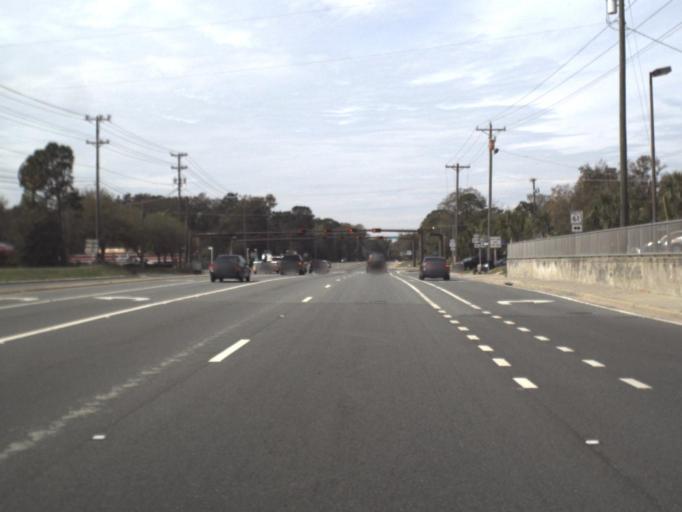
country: US
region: Florida
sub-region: Leon County
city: Tallahassee
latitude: 30.3760
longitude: -84.2908
